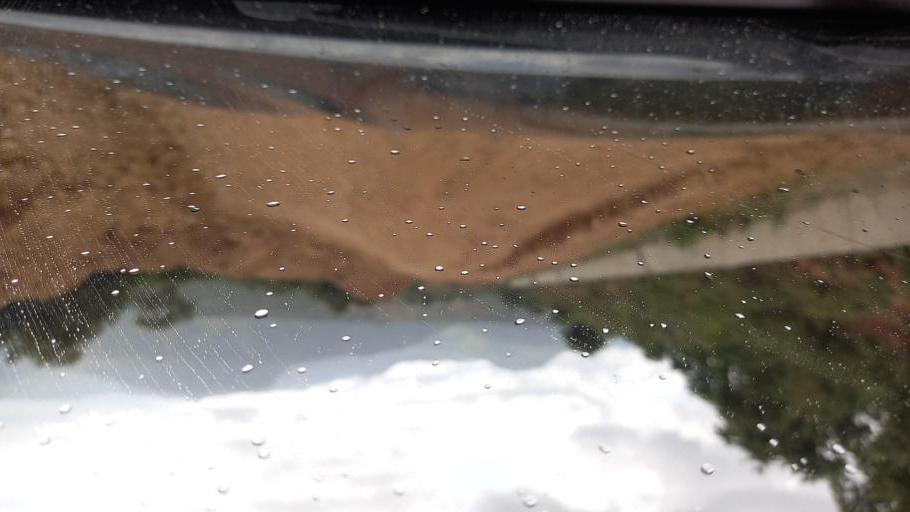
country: ET
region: Southern Nations, Nationalities, and People's Region
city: Mizan Teferi
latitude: 6.1748
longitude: 35.7111
